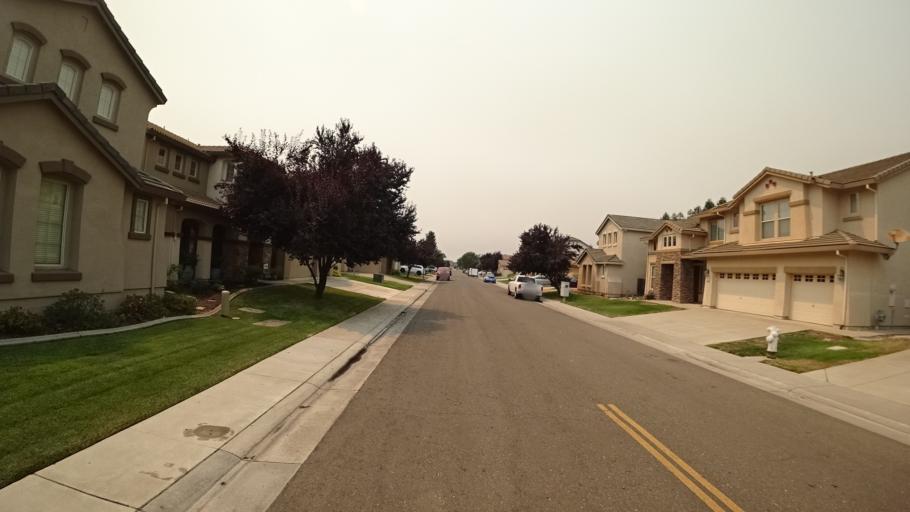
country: US
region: California
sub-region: Sacramento County
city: Laguna
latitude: 38.4019
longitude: -121.4187
